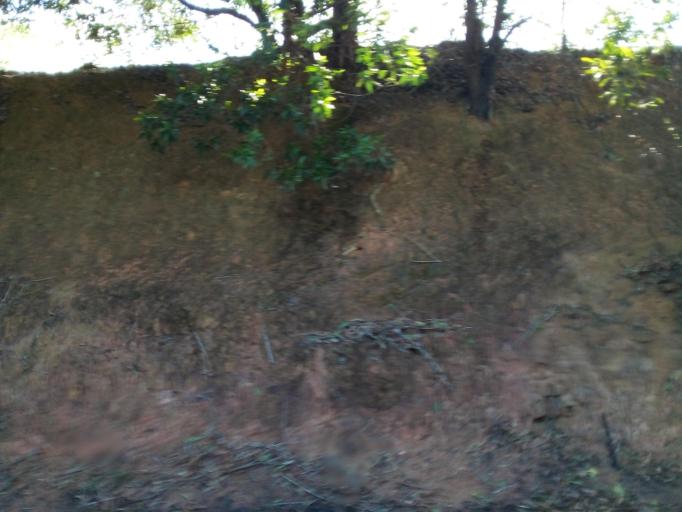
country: BR
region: Espirito Santo
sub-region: Vitoria
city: Vitoria
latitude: -20.2976
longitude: -40.3753
